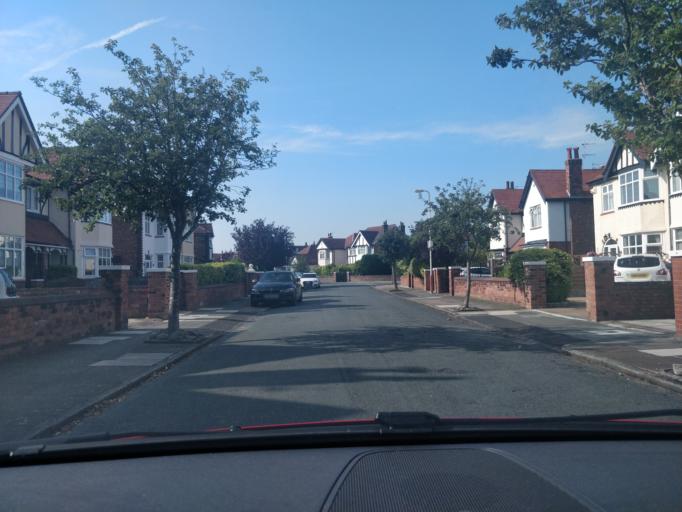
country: GB
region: England
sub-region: Sefton
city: Southport
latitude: 53.6543
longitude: -2.9703
